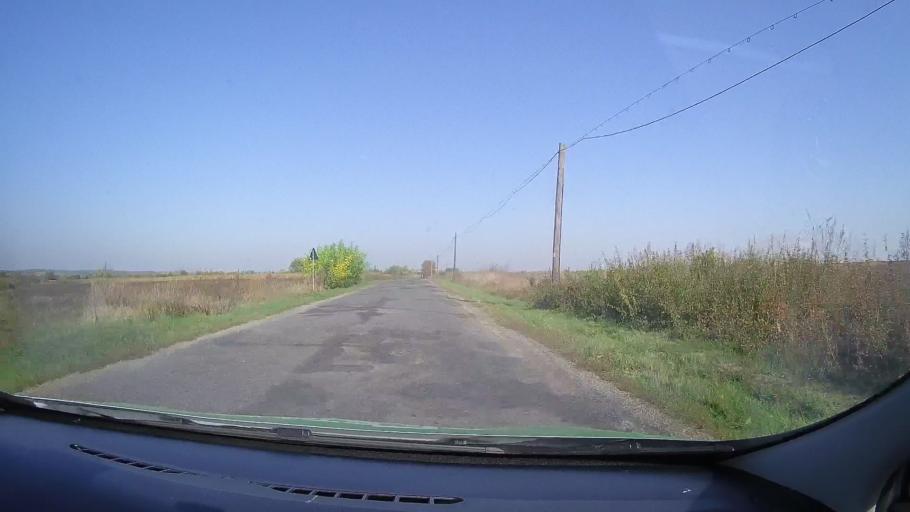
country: RO
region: Satu Mare
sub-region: Comuna Sanislau
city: Sanislau
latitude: 47.6458
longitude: 22.3371
